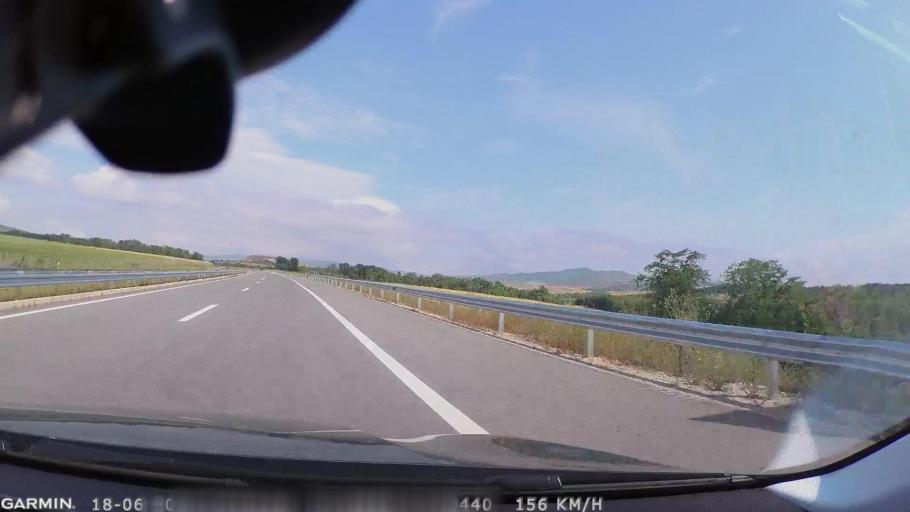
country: MK
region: Sveti Nikole
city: Gorobinci
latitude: 41.9096
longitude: 21.9027
